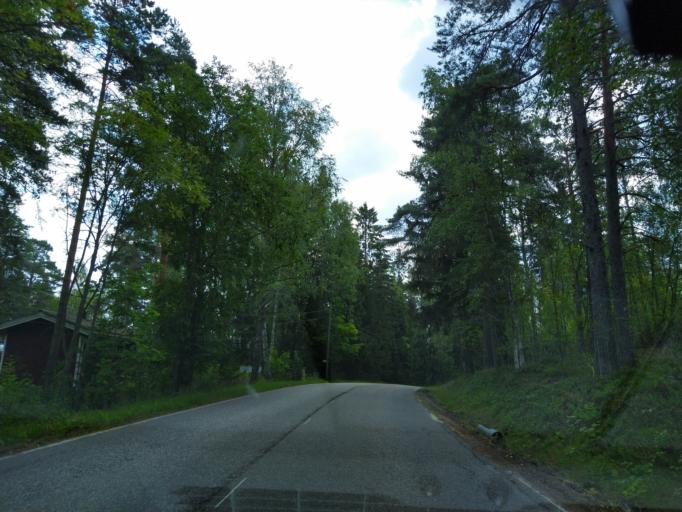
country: FI
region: Uusimaa
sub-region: Helsinki
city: Kirkkonummi
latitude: 60.0965
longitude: 24.4987
